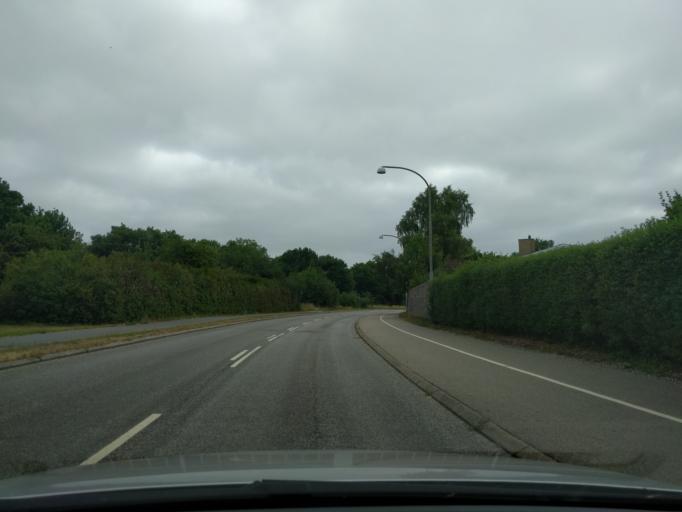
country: DK
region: Capital Region
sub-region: Helsingor Kommune
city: Espergaerde
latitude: 56.0037
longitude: 12.5408
